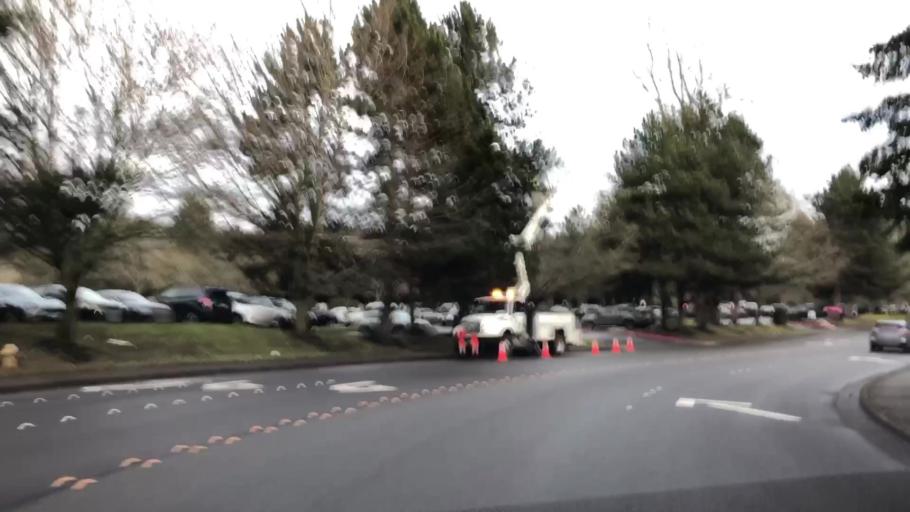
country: US
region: Washington
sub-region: King County
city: Eastgate
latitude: 47.5796
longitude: -122.1317
